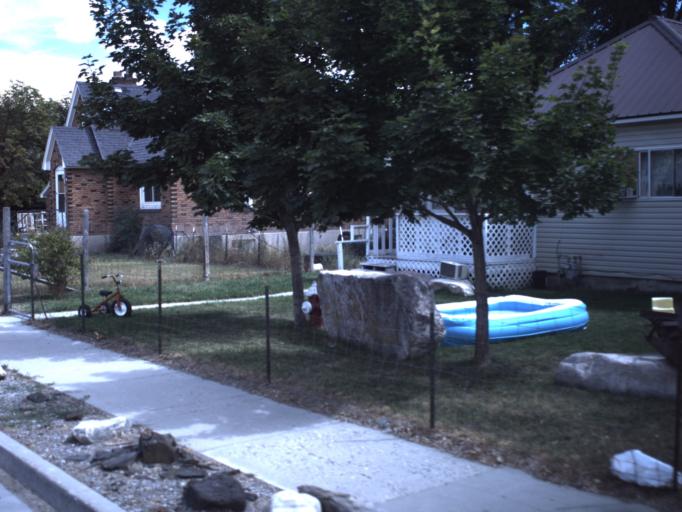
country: US
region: Utah
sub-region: Box Elder County
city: Garland
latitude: 41.7412
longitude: -112.1566
